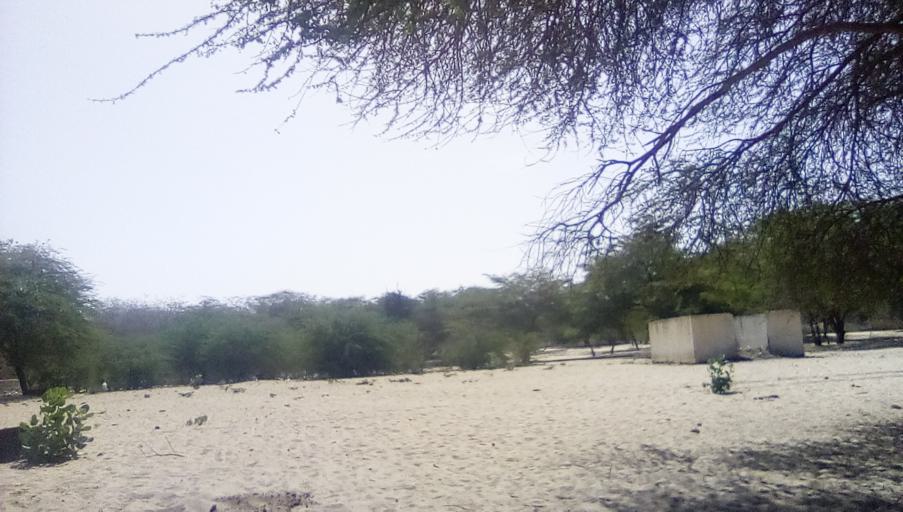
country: SN
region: Saint-Louis
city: Saint-Louis
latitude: 16.0672
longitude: -16.4213
